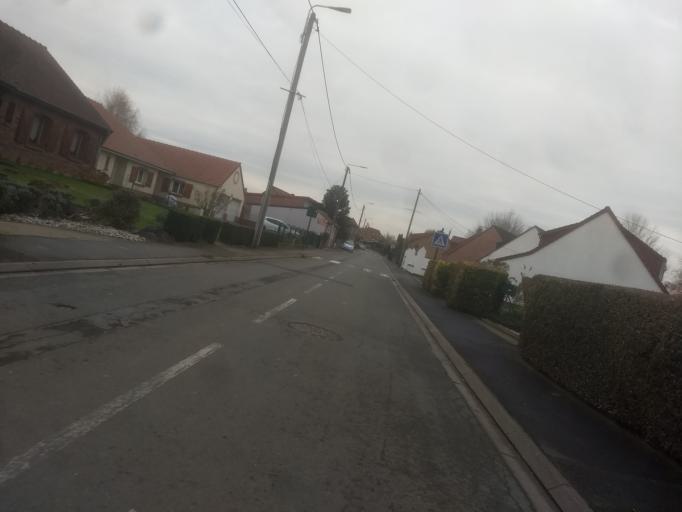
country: FR
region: Nord-Pas-de-Calais
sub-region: Departement du Pas-de-Calais
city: Agny
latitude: 50.2656
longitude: 2.7603
